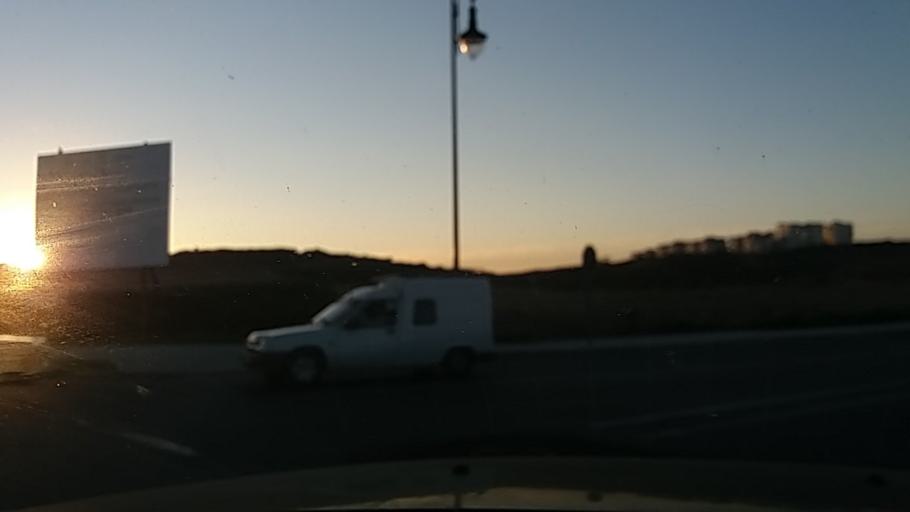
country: MA
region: Tanger-Tetouan
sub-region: Tanger-Assilah
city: Boukhalef
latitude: 35.7573
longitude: -5.9306
